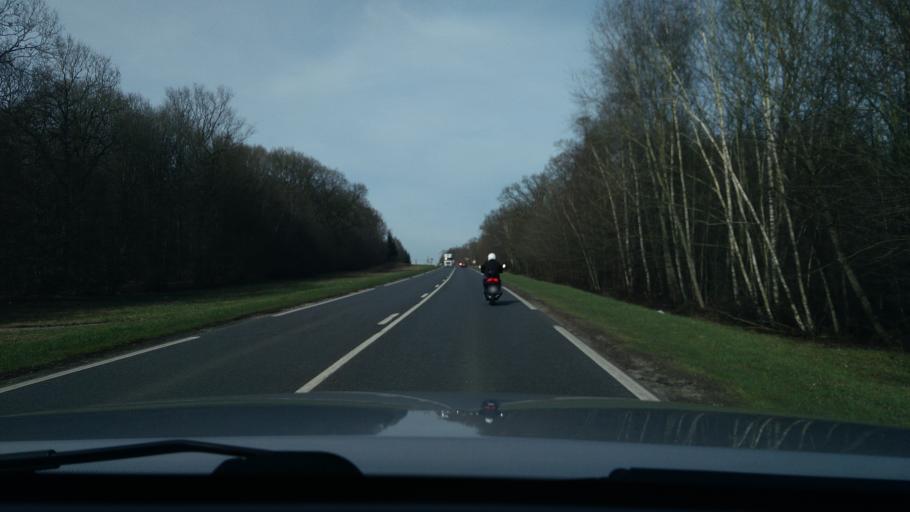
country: FR
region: Ile-de-France
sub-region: Departement de Seine-et-Marne
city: Guignes
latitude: 48.6611
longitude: 2.8093
